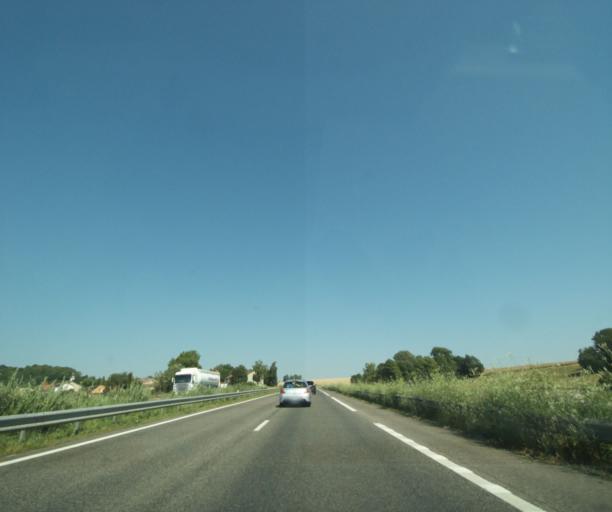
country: FR
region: Lorraine
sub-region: Departement de la Meuse
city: Vacon
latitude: 48.7017
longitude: 5.5332
